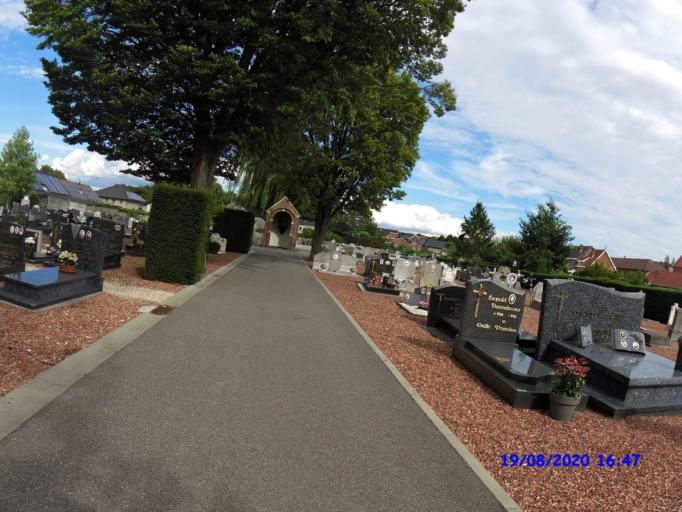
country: BE
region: Flanders
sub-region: Provincie Limburg
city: Nieuwerkerken
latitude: 50.8645
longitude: 5.1945
